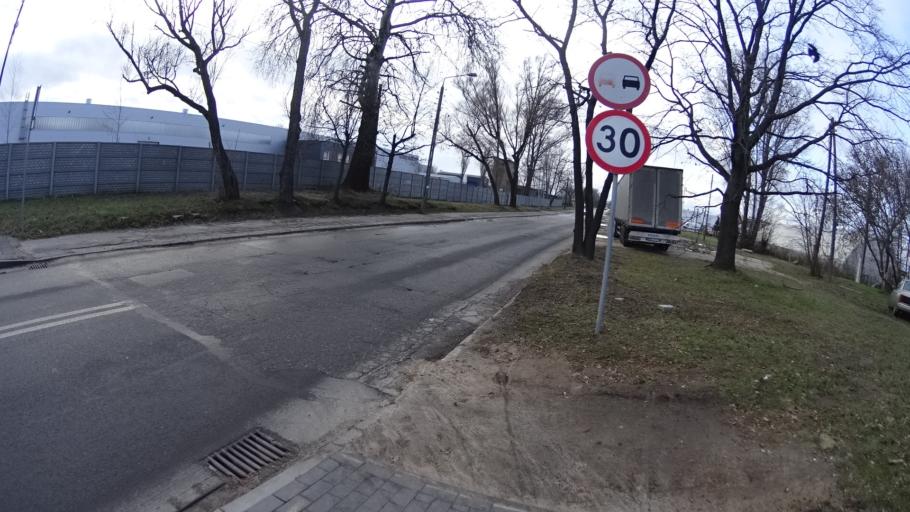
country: PL
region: Masovian Voivodeship
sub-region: Powiat pruszkowski
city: Pruszkow
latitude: 52.1656
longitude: 20.7777
